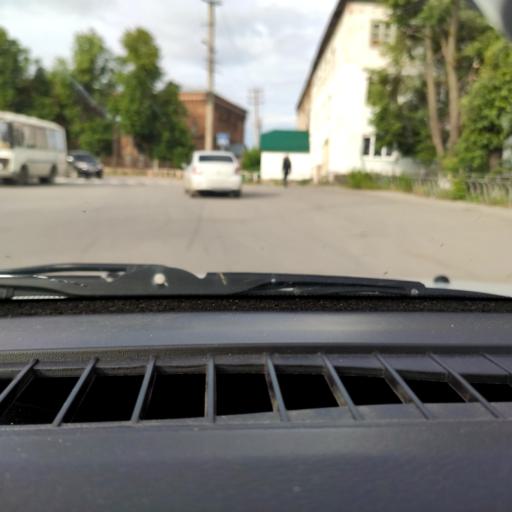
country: RU
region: Perm
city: Kungur
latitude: 57.4240
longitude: 56.9541
